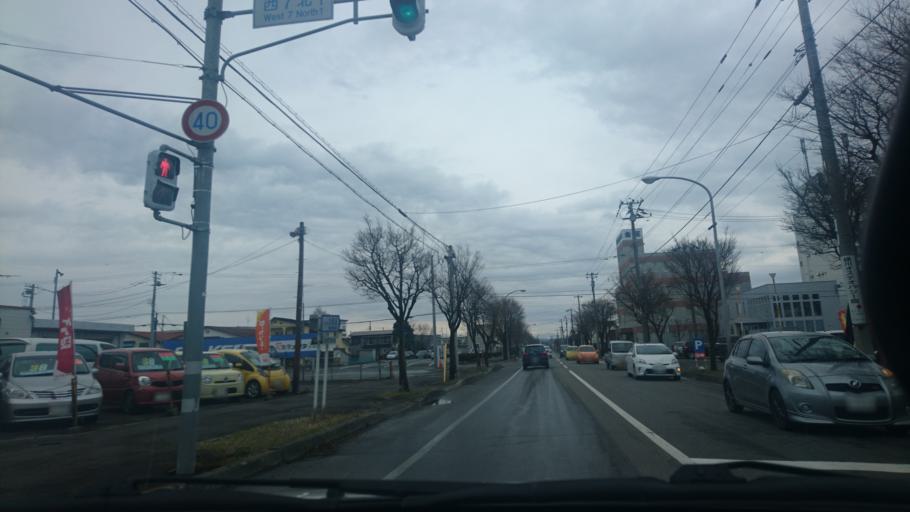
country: JP
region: Hokkaido
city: Obihiro
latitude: 42.9313
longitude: 143.1929
